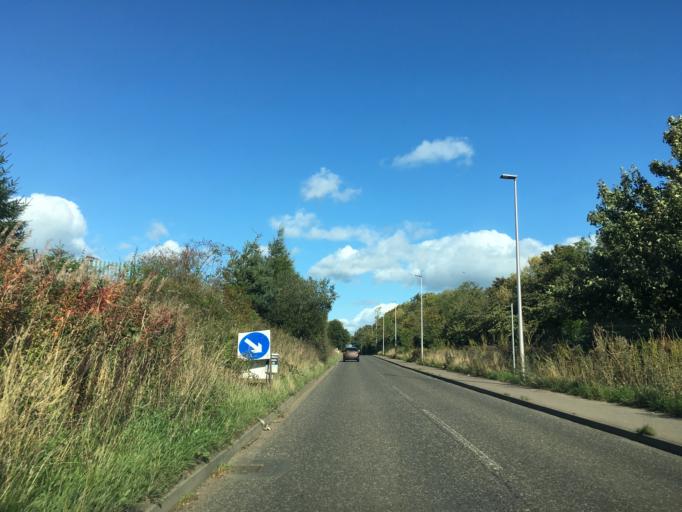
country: GB
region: Scotland
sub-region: Midlothian
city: Bonnyrigg
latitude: 55.9188
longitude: -3.1152
